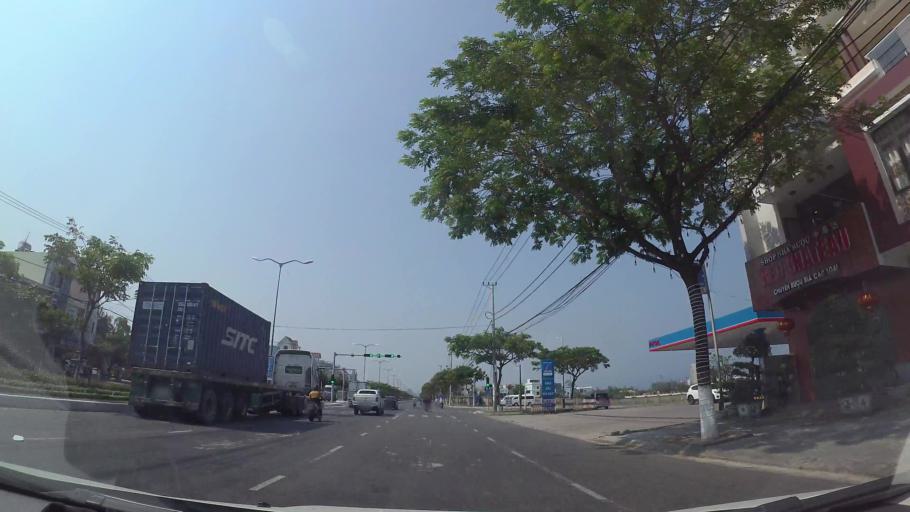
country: VN
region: Da Nang
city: Ngu Hanh Son
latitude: 16.0188
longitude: 108.2531
